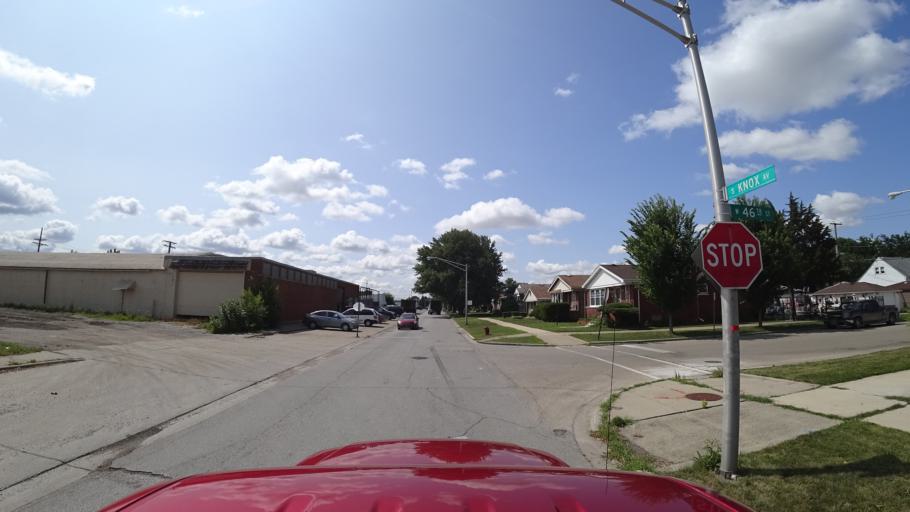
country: US
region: Illinois
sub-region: Cook County
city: Cicero
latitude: 41.8097
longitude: -87.7396
